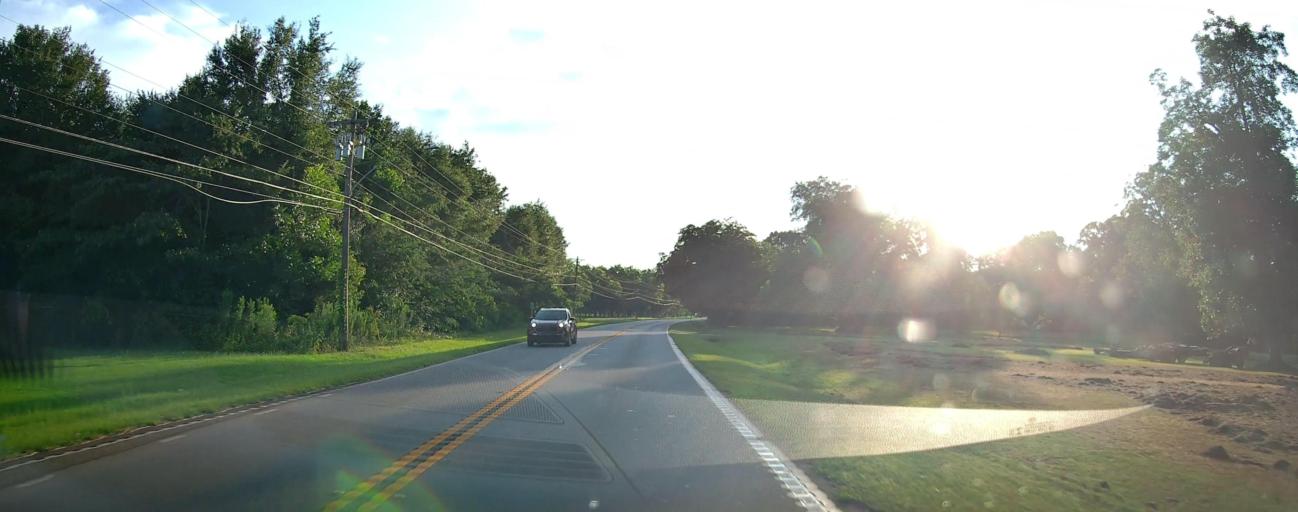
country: US
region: Georgia
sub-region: Peach County
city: Fort Valley
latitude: 32.5578
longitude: -83.9017
